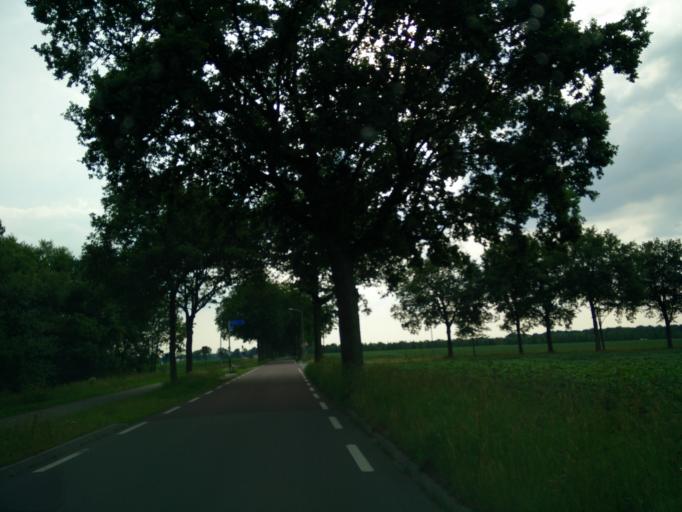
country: NL
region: Drenthe
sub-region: Gemeente Aa en Hunze
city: Anloo
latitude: 52.9904
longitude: 6.6880
